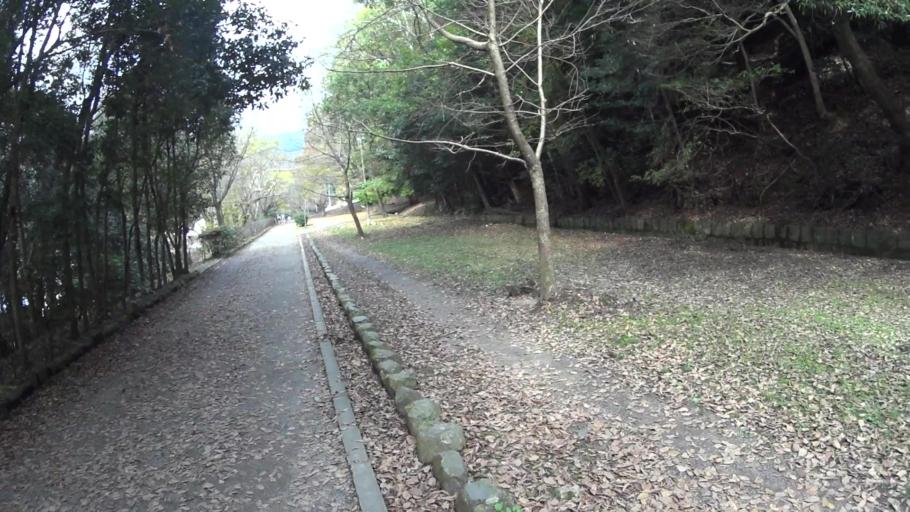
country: JP
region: Shiga Prefecture
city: Otsu-shi
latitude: 34.9947
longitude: 135.8210
